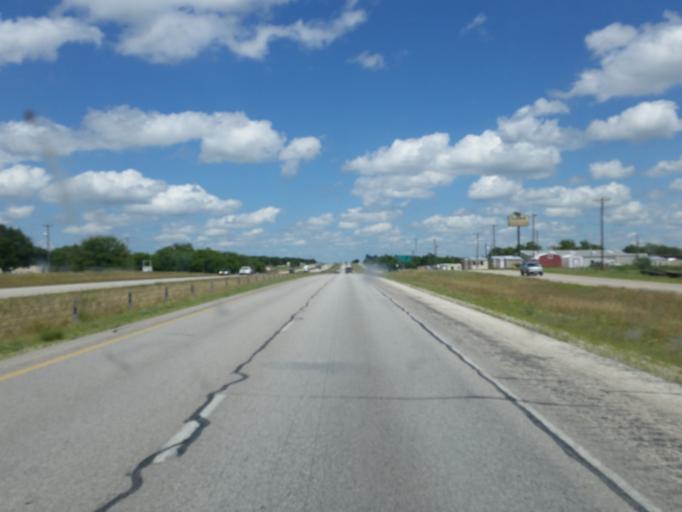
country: US
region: Texas
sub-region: Callahan County
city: Clyde
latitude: 32.4101
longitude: -99.4757
